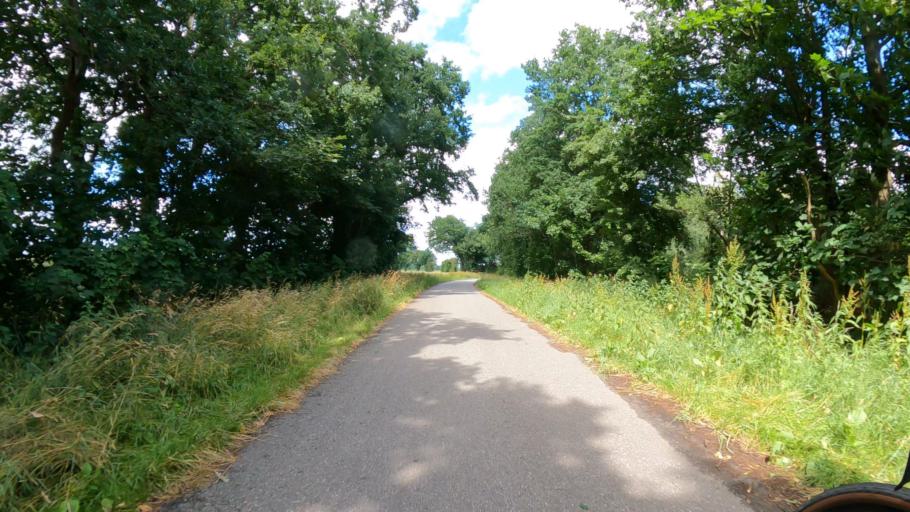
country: DE
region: Lower Saxony
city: Neu Wulmstorf
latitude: 53.4549
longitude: 9.7591
